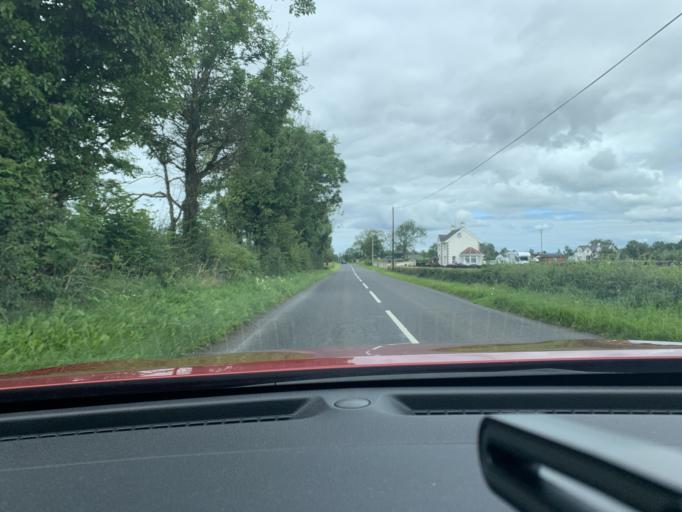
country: GB
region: Northern Ireland
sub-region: Fermanagh District
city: Enniskillen
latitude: 54.2706
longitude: -7.7047
